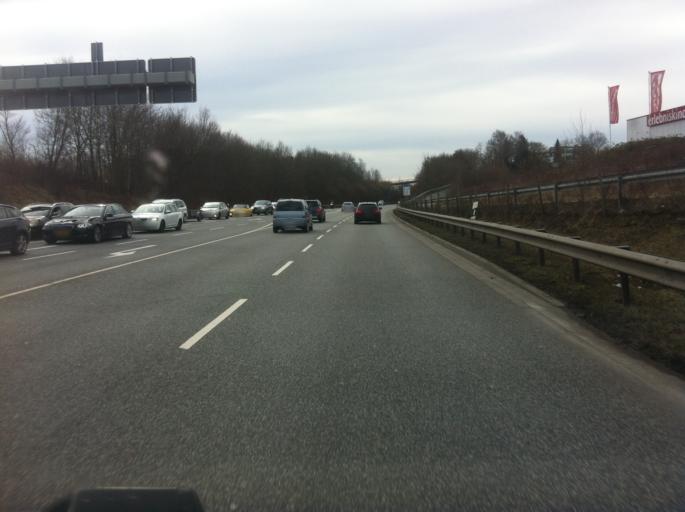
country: DE
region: Rheinland-Pfalz
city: Mendig
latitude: 50.3815
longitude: 7.2708
